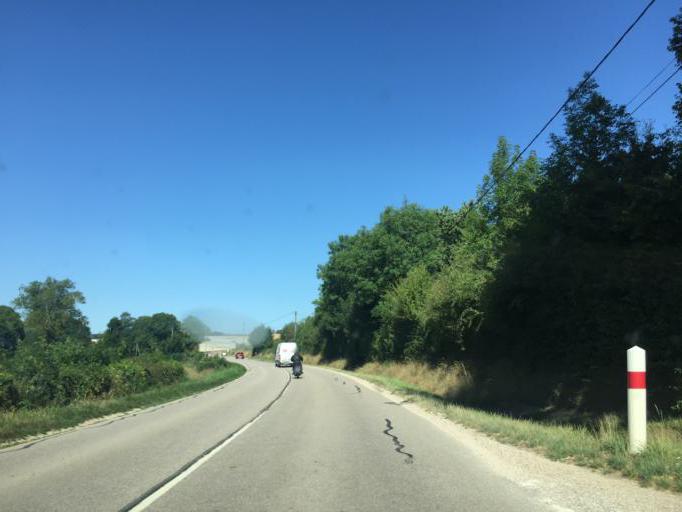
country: FR
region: Bourgogne
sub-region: Departement de la Nievre
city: Clamecy
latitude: 47.4563
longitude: 3.4665
